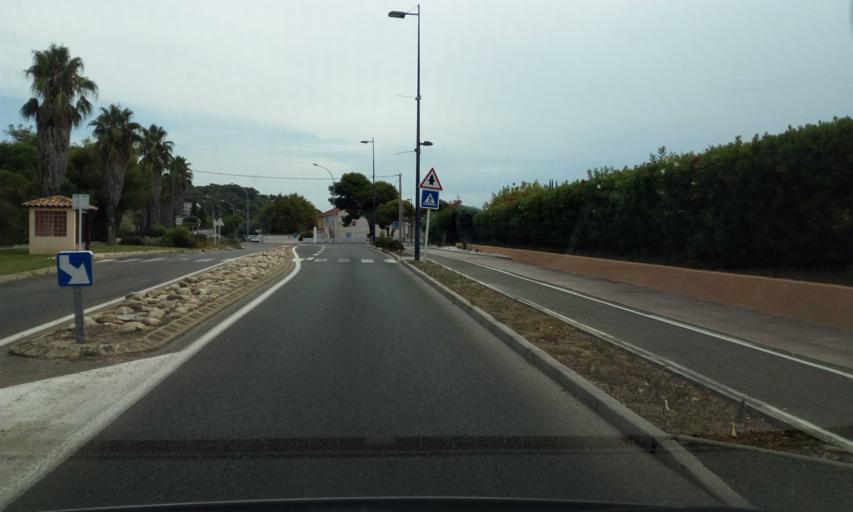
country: FR
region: Provence-Alpes-Cote d'Azur
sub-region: Departement du Var
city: Carqueiranne
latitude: 43.0904
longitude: 6.0833
